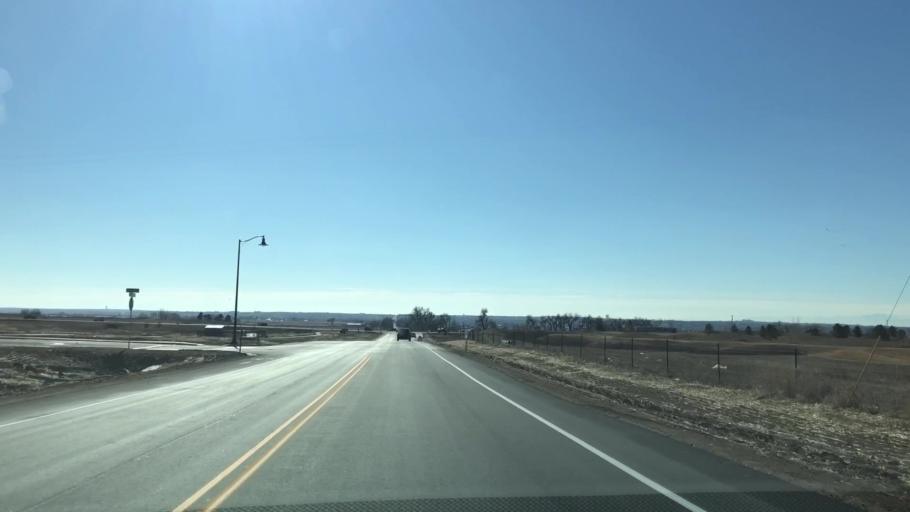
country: US
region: Colorado
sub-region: Weld County
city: Windsor
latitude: 40.5269
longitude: -104.9442
